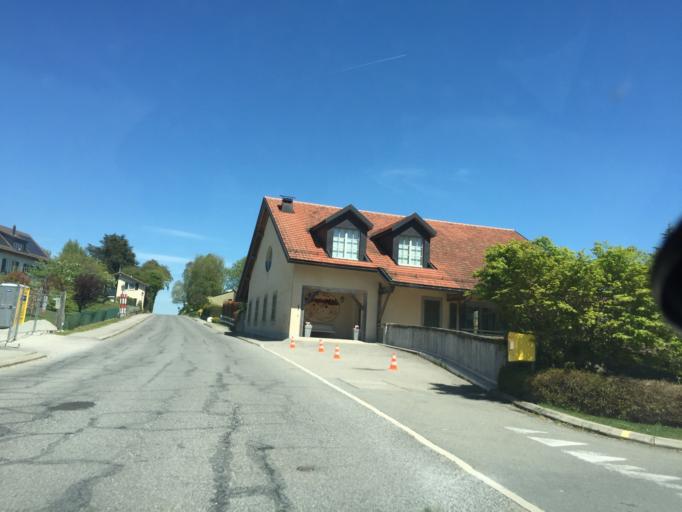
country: CH
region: Vaud
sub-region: Morges District
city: Apples
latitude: 46.5539
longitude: 6.4311
